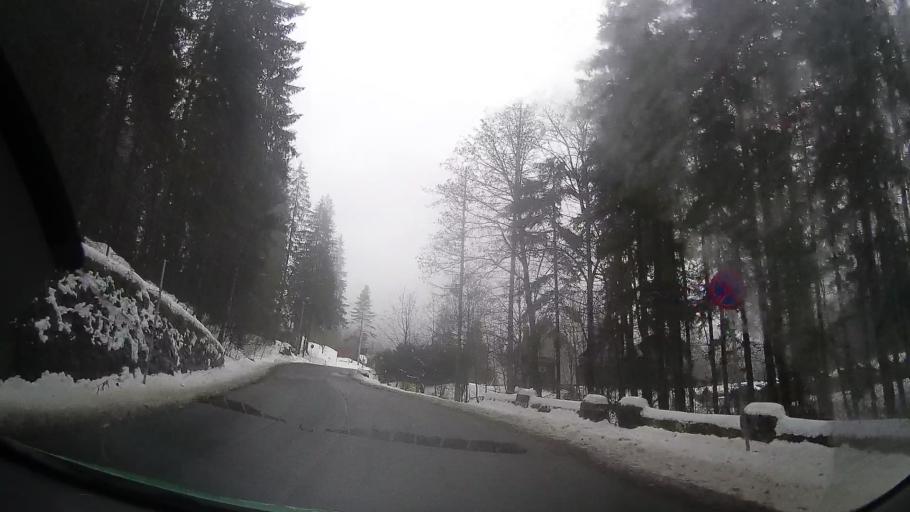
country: RO
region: Neamt
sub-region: Comuna Bicaz Chei
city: Bicaz Chei
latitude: 46.7915
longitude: 25.7910
